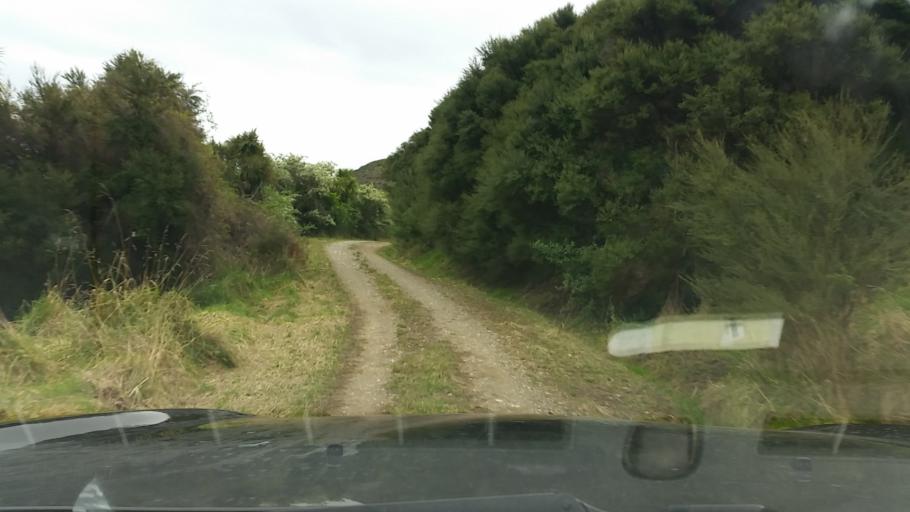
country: NZ
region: Marlborough
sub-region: Marlborough District
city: Blenheim
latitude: -41.8856
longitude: 174.0845
